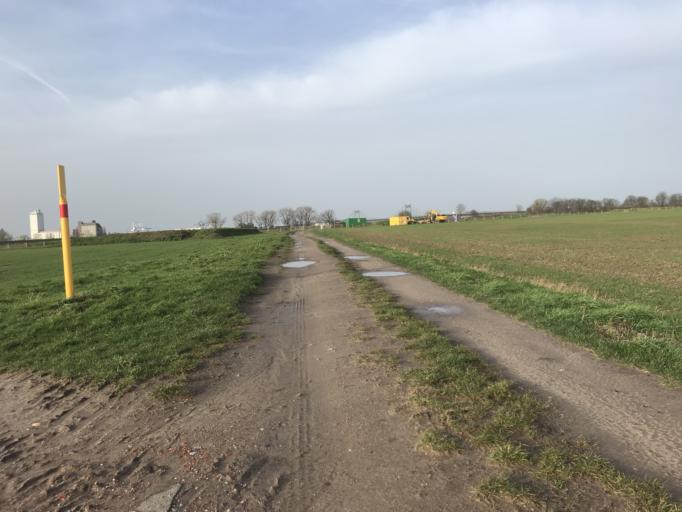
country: DE
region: North Rhine-Westphalia
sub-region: Regierungsbezirk Dusseldorf
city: Meerbusch
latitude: 51.3521
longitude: 6.6799
